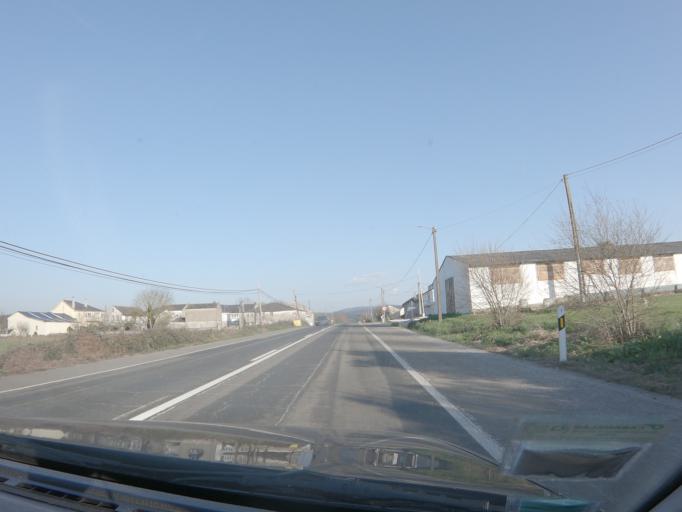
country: ES
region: Galicia
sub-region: Provincia de Lugo
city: Corgo
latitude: 42.9345
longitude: -7.4038
